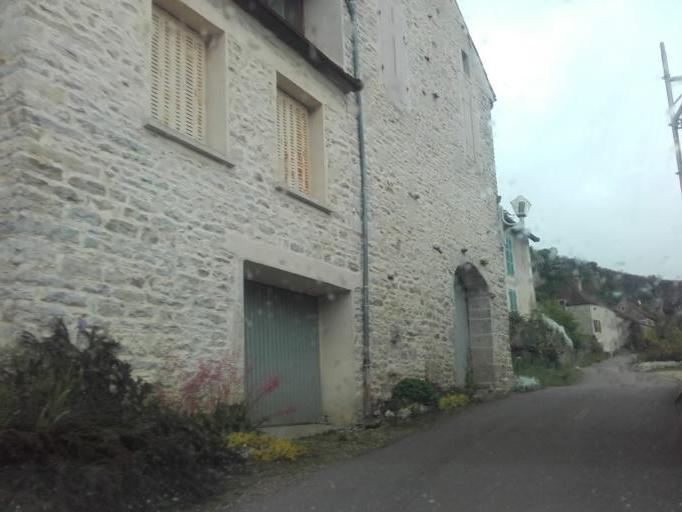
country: FR
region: Bourgogne
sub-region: Departement de la Cote-d'Or
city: Nolay
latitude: 46.9883
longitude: 4.6866
